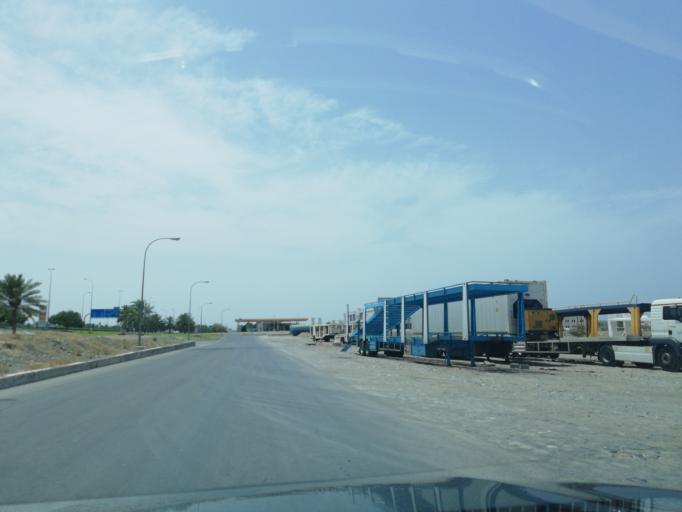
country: OM
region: Muhafazat Masqat
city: As Sib al Jadidah
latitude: 23.6567
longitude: 58.2015
